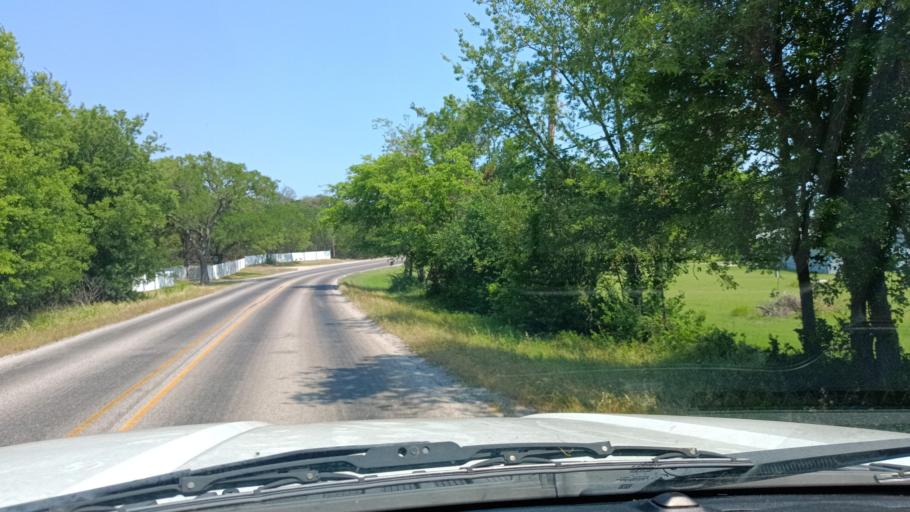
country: US
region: Texas
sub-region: Bell County
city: Morgans Point Resort
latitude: 31.1095
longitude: -97.5238
